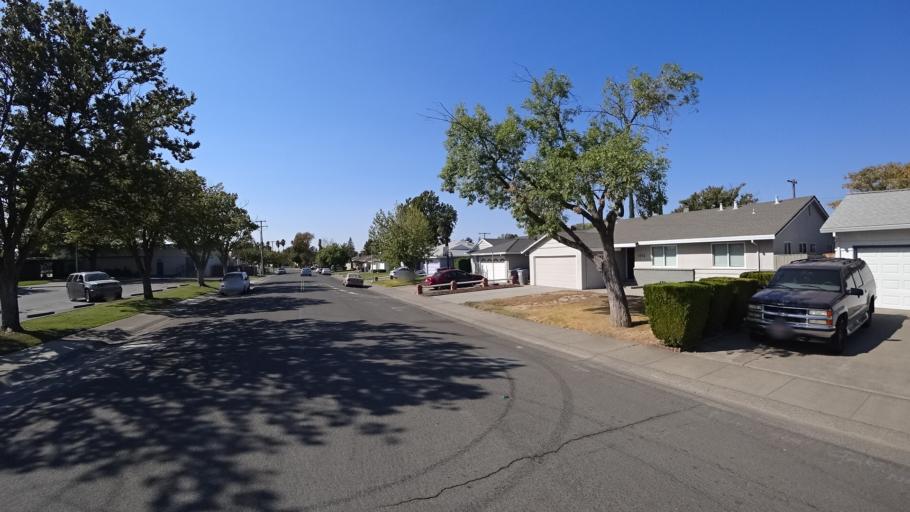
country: US
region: California
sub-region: Sacramento County
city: Parkway
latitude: 38.4929
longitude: -121.4964
